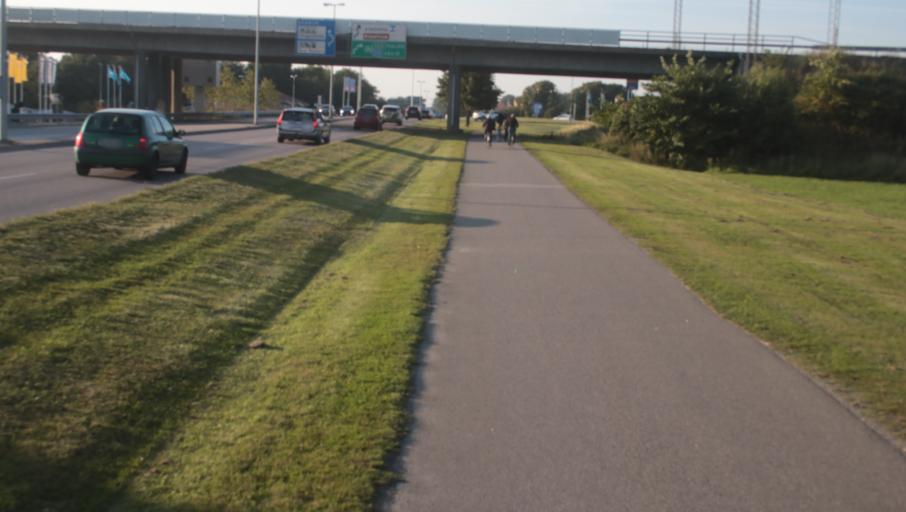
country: SE
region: Blekinge
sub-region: Karlshamns Kommun
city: Karlshamn
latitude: 56.1876
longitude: 14.8479
